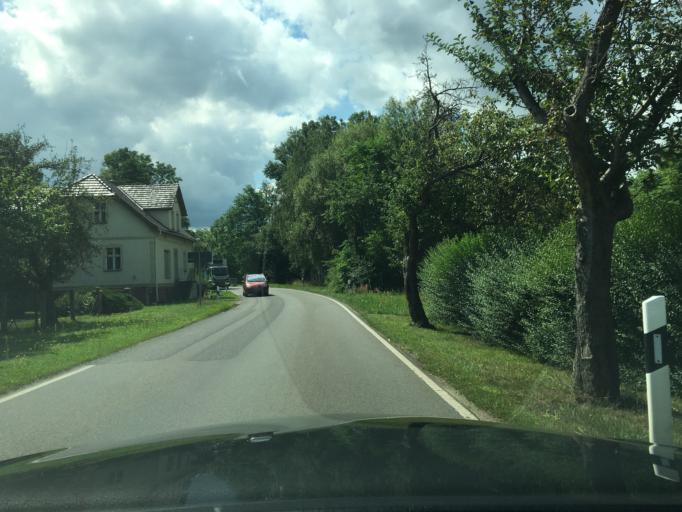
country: DE
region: Brandenburg
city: Burg
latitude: 51.8482
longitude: 14.1029
